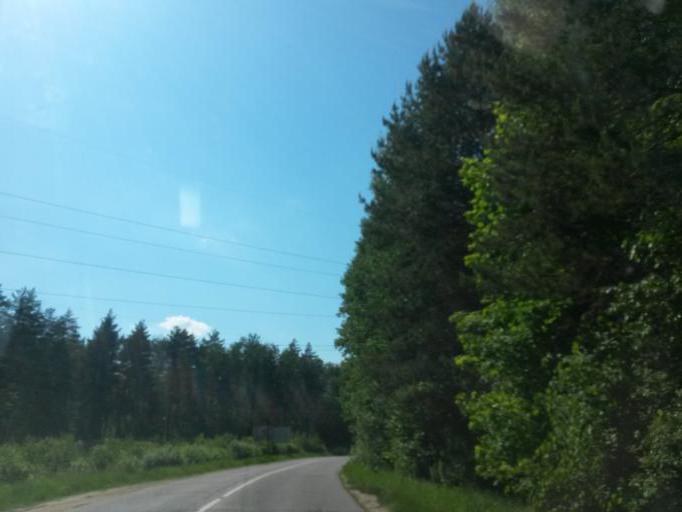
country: RU
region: Moskovskaya
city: Danki
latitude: 54.9055
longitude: 37.5190
